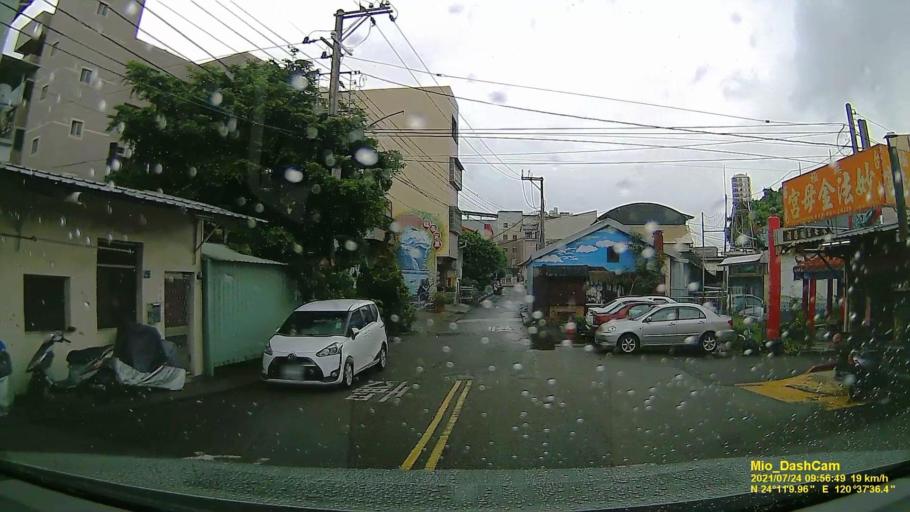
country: TW
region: Taiwan
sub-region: Taichung City
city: Taichung
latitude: 24.1862
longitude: 120.6268
